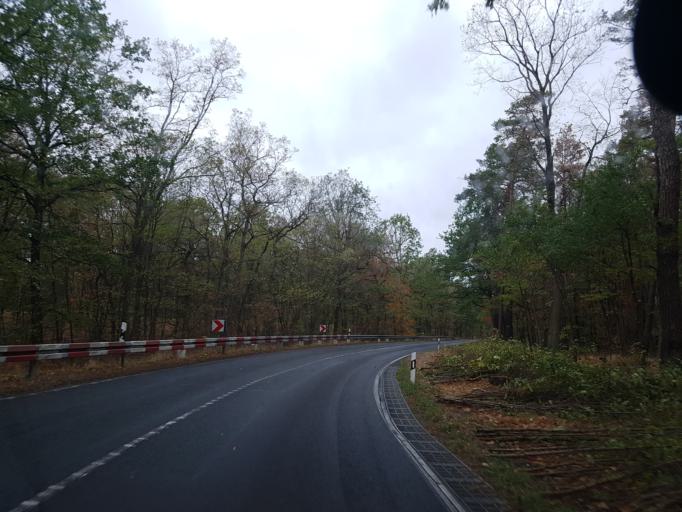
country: DE
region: Brandenburg
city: Falkenberg
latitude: 51.6139
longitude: 13.2345
